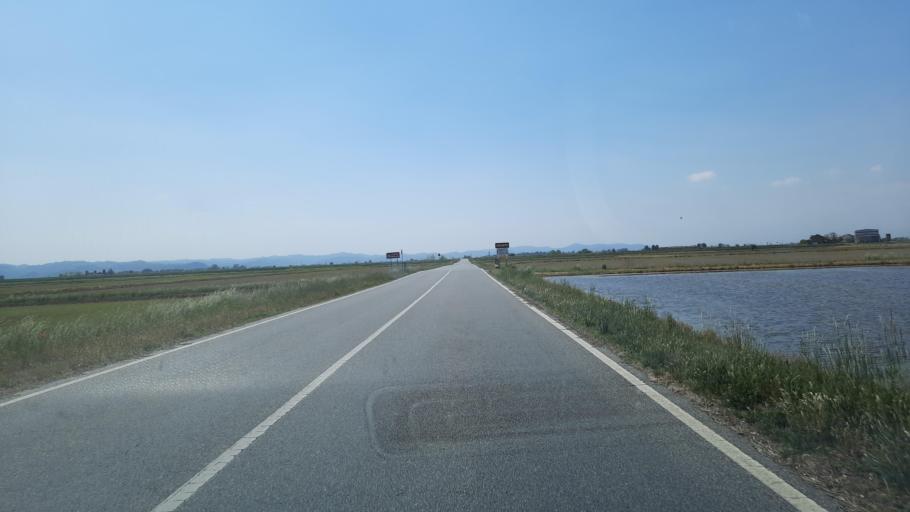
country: IT
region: Piedmont
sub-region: Provincia di Vercelli
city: Fontanetto Po
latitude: 45.2309
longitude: 8.1578
